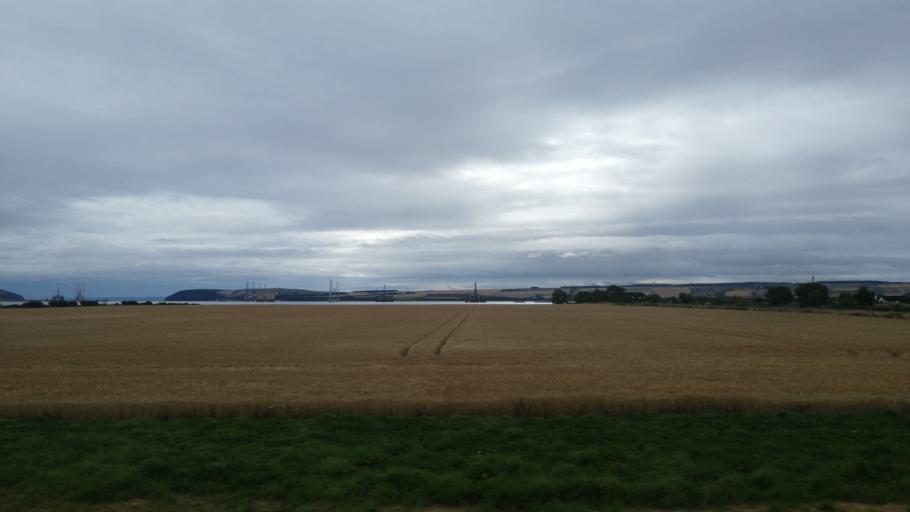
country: GB
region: Scotland
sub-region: Highland
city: Invergordon
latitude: 57.7075
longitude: -4.1388
